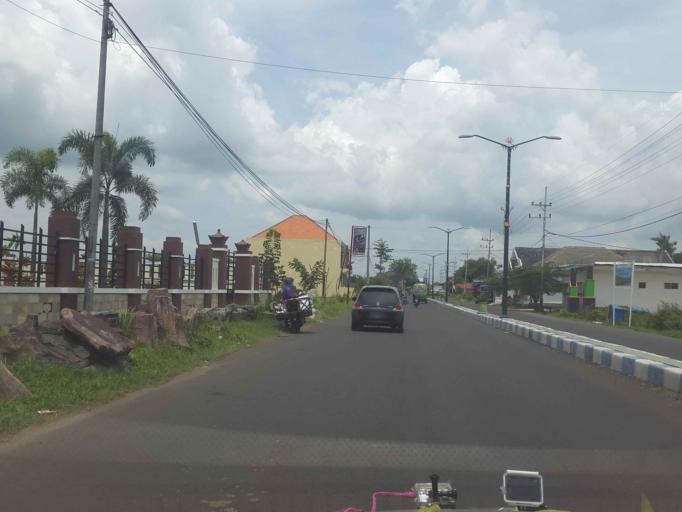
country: ID
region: East Java
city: Sumenep
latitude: -7.0338
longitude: 113.8508
